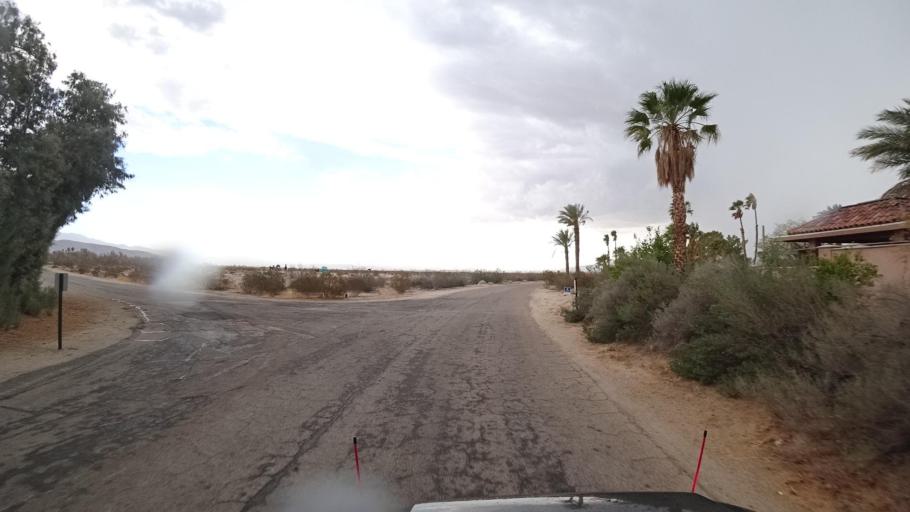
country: US
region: California
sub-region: San Diego County
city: Borrego Springs
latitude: 33.2903
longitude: -116.3820
